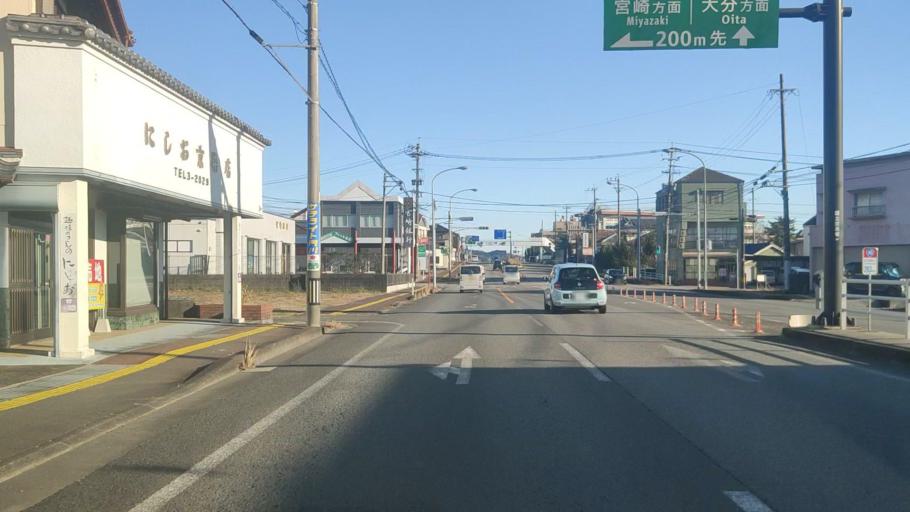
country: JP
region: Miyazaki
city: Nobeoka
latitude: 32.4707
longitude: 131.6503
